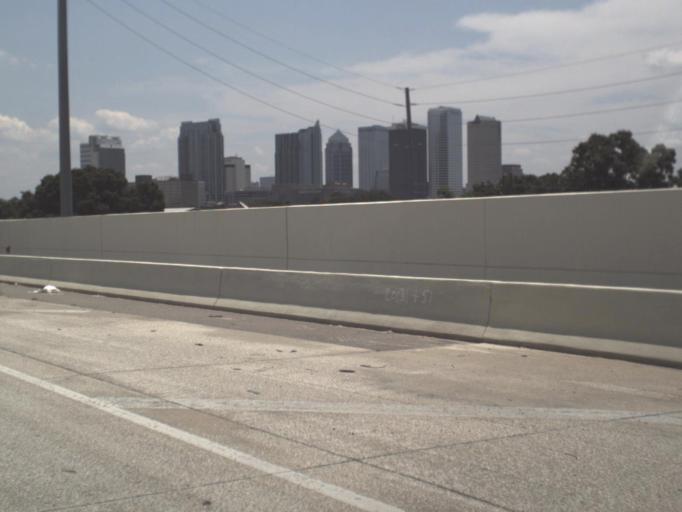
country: US
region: Florida
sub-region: Hillsborough County
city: Tampa
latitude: 27.9555
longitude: -82.4714
